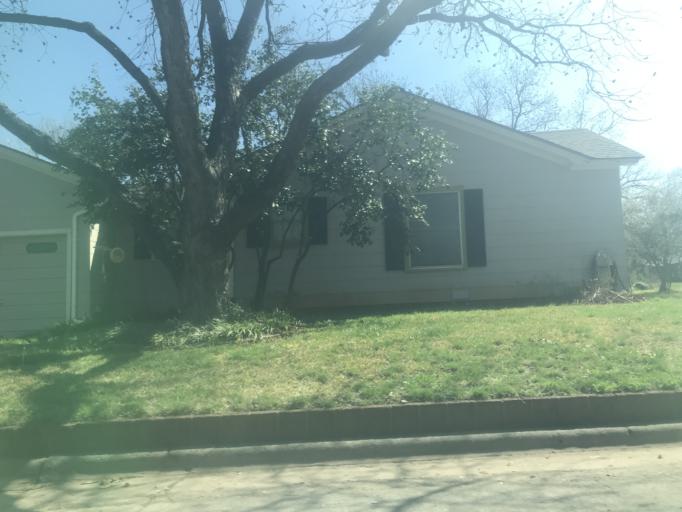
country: US
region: Texas
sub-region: Taylor County
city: Abilene
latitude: 32.4424
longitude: -99.7744
